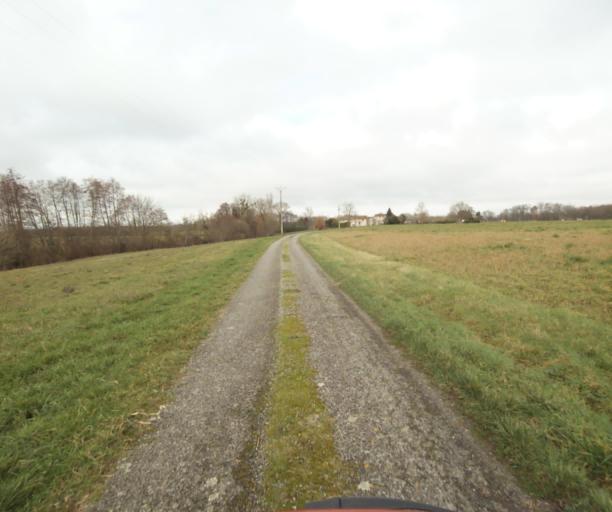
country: FR
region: Midi-Pyrenees
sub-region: Departement de l'Ariege
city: La Tour-du-Crieu
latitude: 43.1592
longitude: 1.6945
